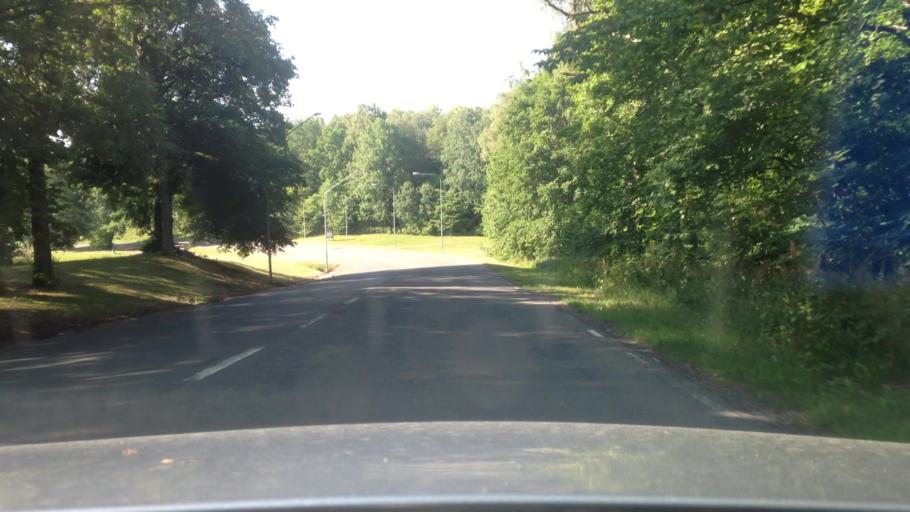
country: SE
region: Vaestra Goetaland
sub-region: Skovde Kommun
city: Skoevde
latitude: 58.3982
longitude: 13.8185
